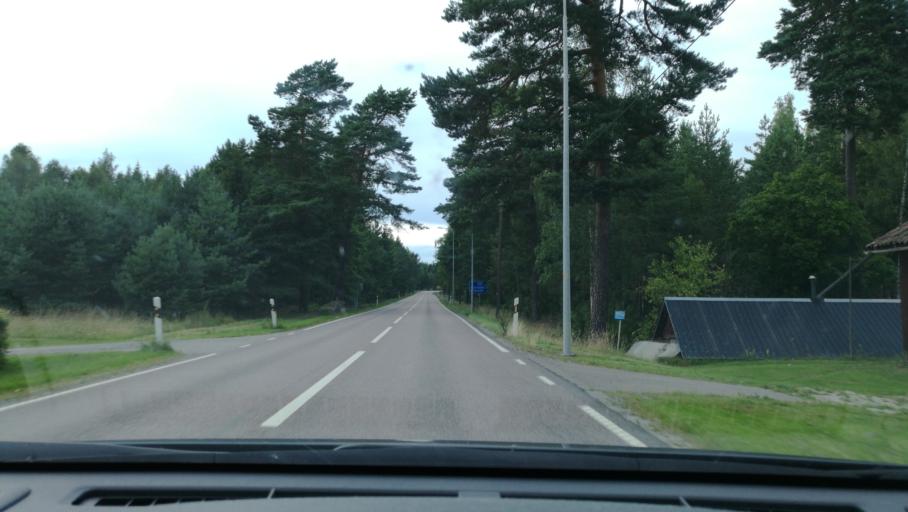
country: SE
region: Vaestmanland
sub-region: Kungsors Kommun
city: Kungsoer
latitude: 59.2845
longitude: 16.1160
